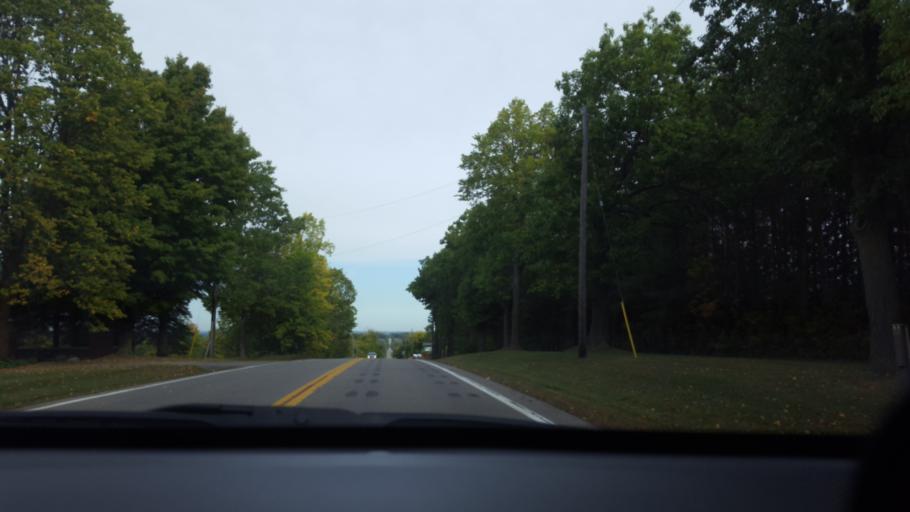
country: CA
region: Ontario
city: Newmarket
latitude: 43.9868
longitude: -79.5440
